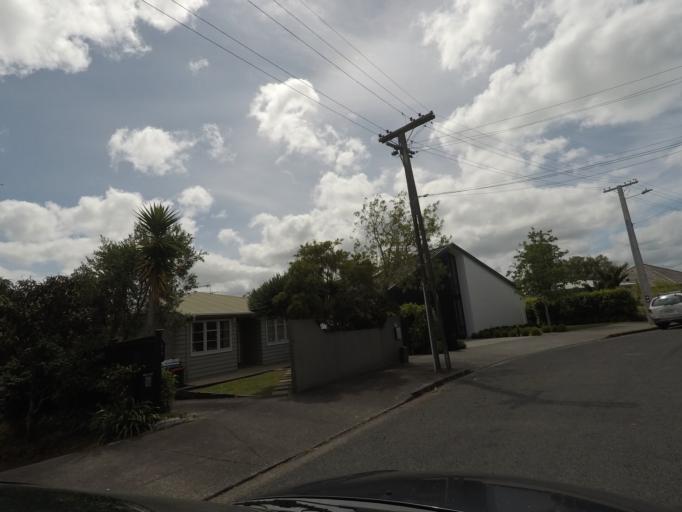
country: NZ
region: Auckland
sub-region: Auckland
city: Rosebank
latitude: -36.8542
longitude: 174.7152
